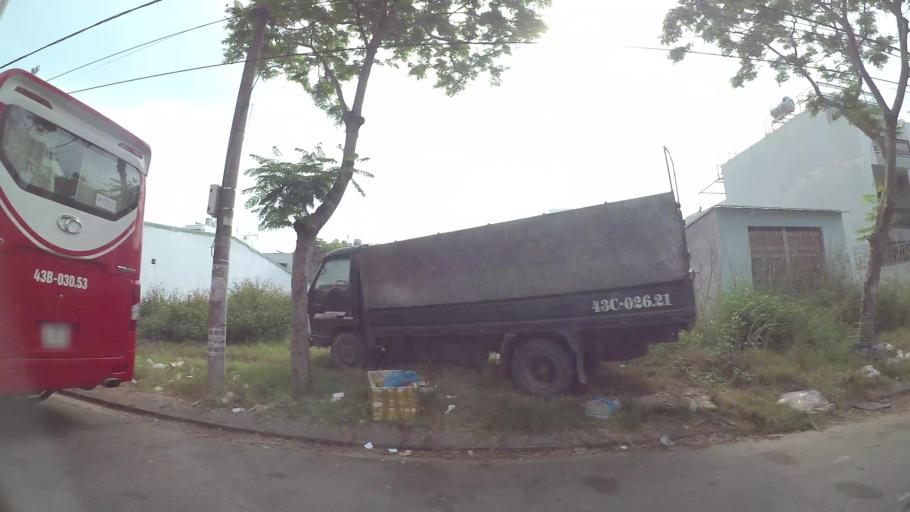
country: VN
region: Da Nang
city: Son Tra
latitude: 16.0862
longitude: 108.2465
